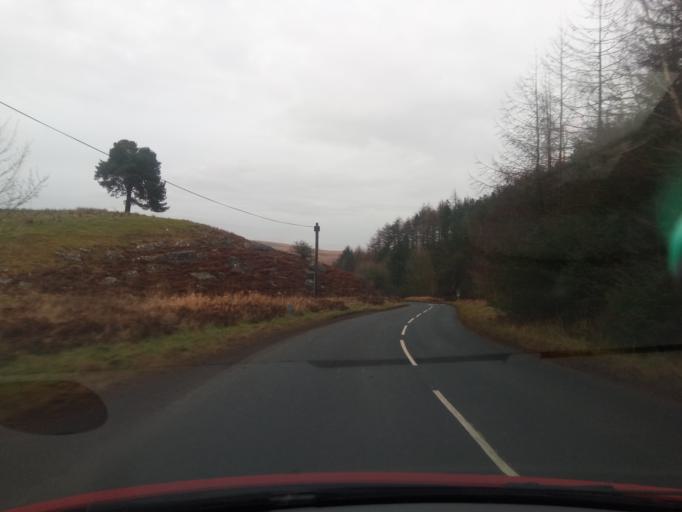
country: GB
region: England
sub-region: Northumberland
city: Haltwhistle
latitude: 55.1778
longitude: -2.4521
